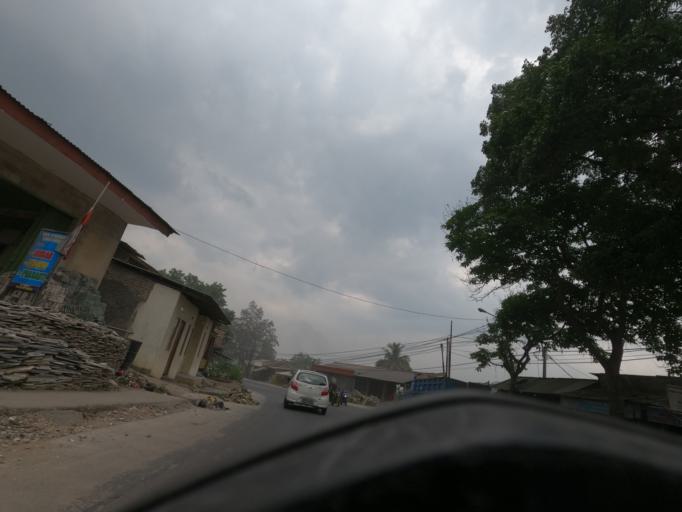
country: ID
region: West Java
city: Padalarang
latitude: -6.8313
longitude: 107.4500
